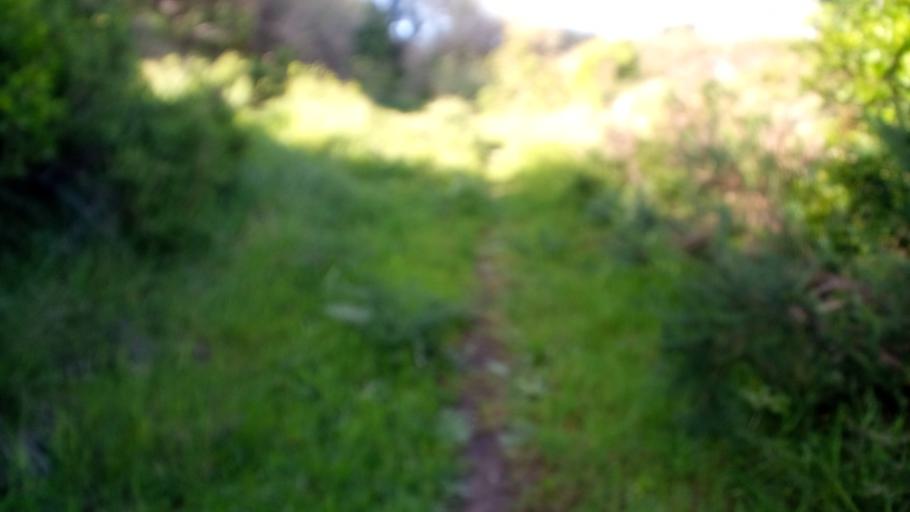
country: PT
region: Leiria
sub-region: Caldas da Rainha
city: Caldas da Rainha
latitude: 39.4517
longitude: -9.1957
